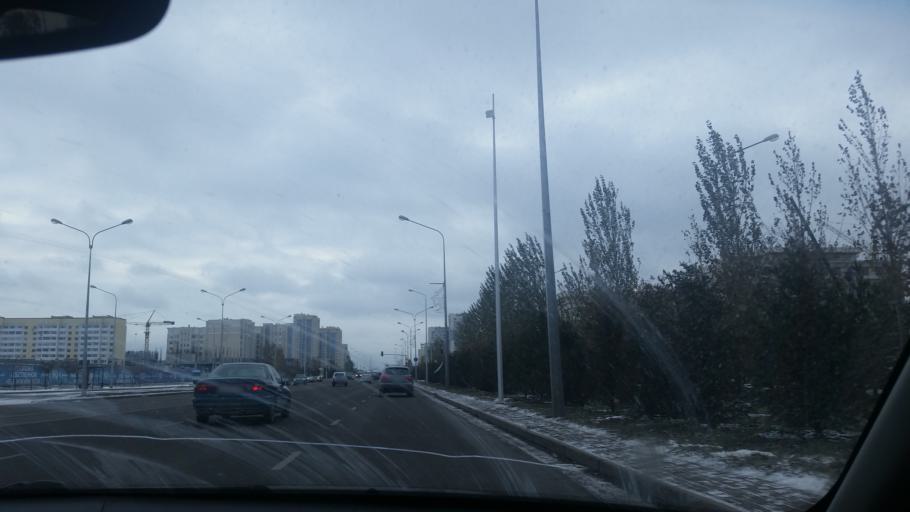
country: KZ
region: Astana Qalasy
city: Astana
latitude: 51.1019
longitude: 71.4291
